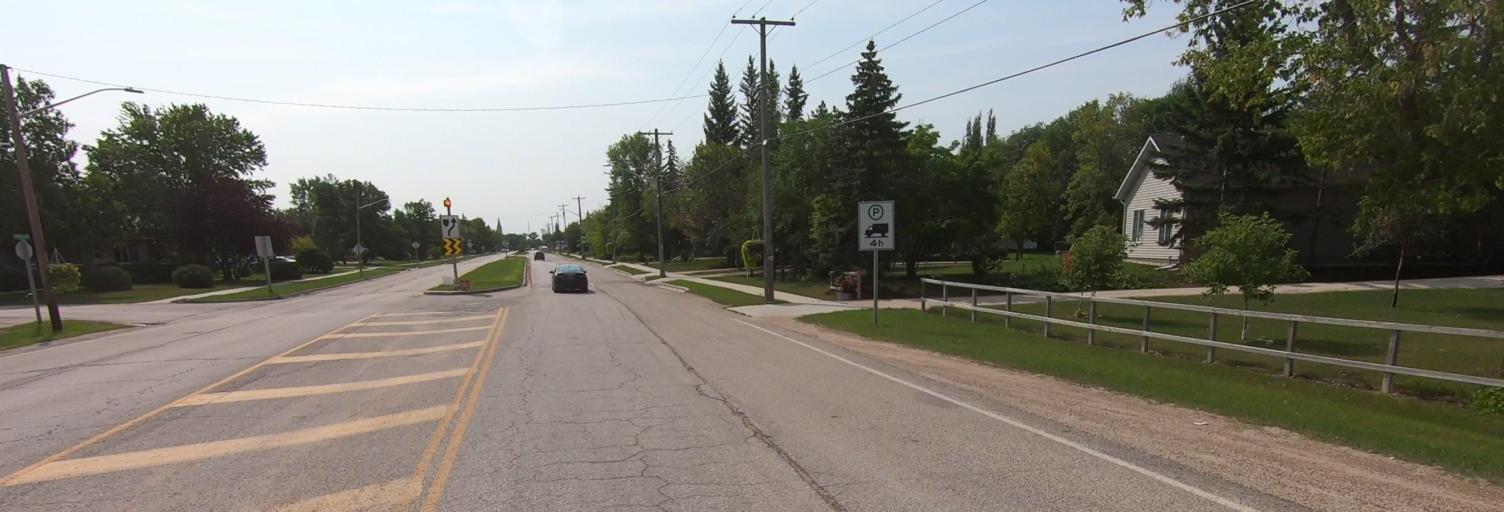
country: CA
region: Manitoba
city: Niverville
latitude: 49.6794
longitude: -97.1144
